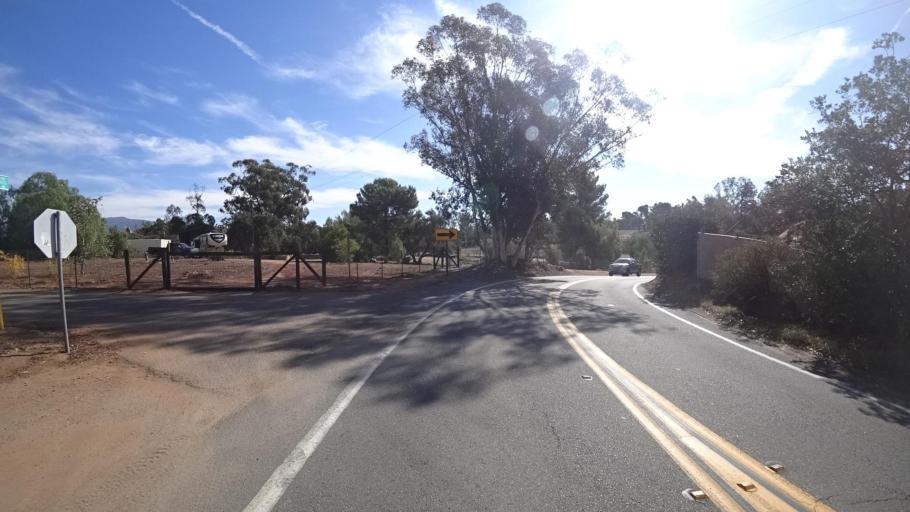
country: US
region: California
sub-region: San Diego County
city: Harbison Canyon
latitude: 32.8190
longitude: -116.7981
